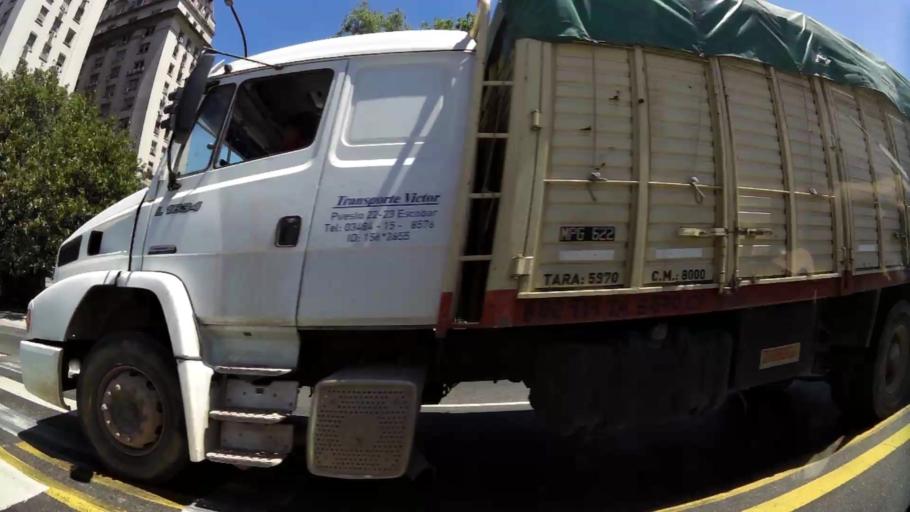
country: AR
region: Buenos Aires F.D.
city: Buenos Aires
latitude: -34.6088
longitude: -58.3677
